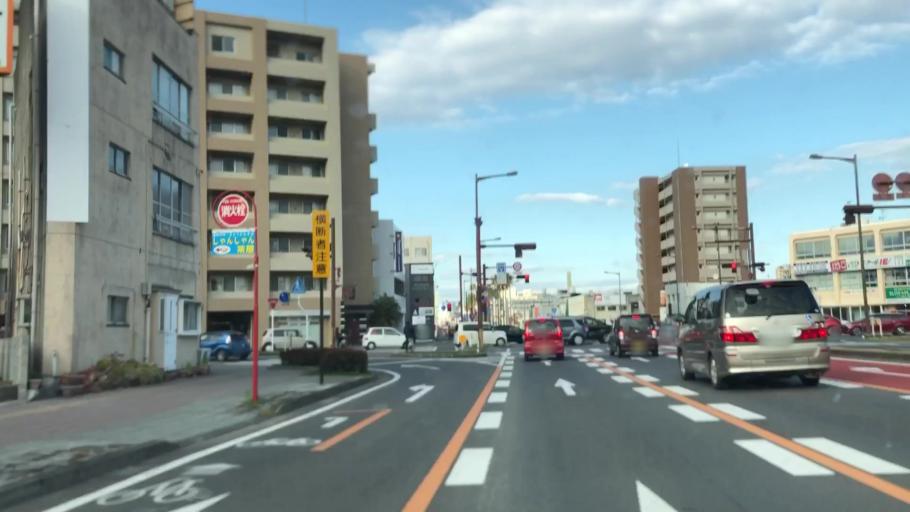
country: JP
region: Miyazaki
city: Miyazaki-shi
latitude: 31.8976
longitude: 131.4178
